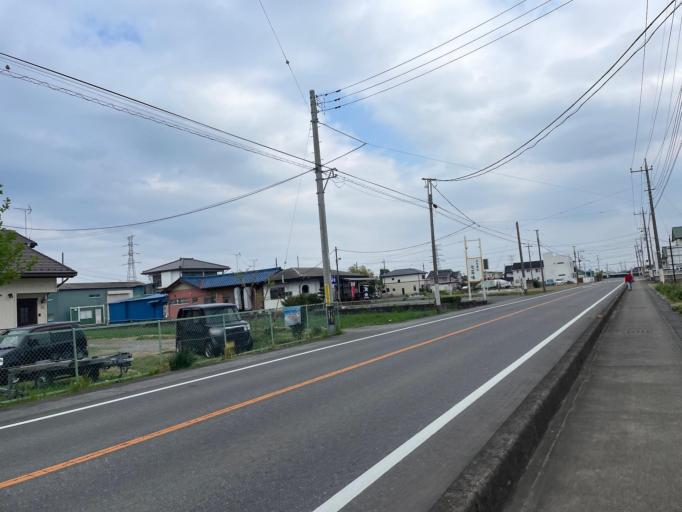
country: JP
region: Gunma
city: Isesaki
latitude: 36.2808
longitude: 139.2032
